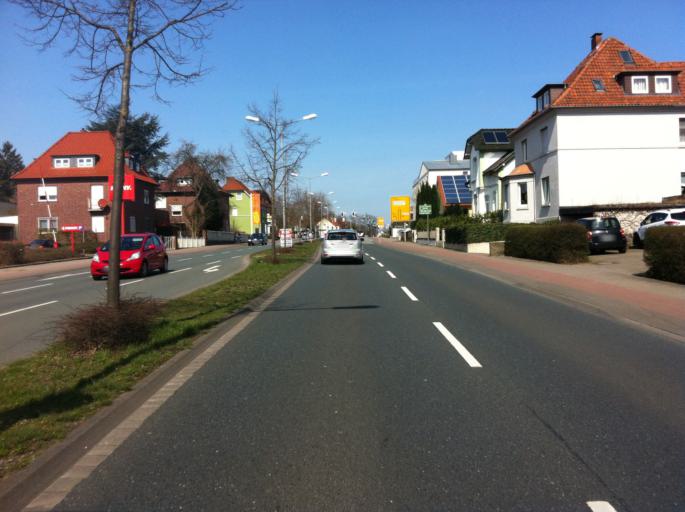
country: DE
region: North Rhine-Westphalia
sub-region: Regierungsbezirk Detmold
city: Minden
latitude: 52.2864
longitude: 8.9012
